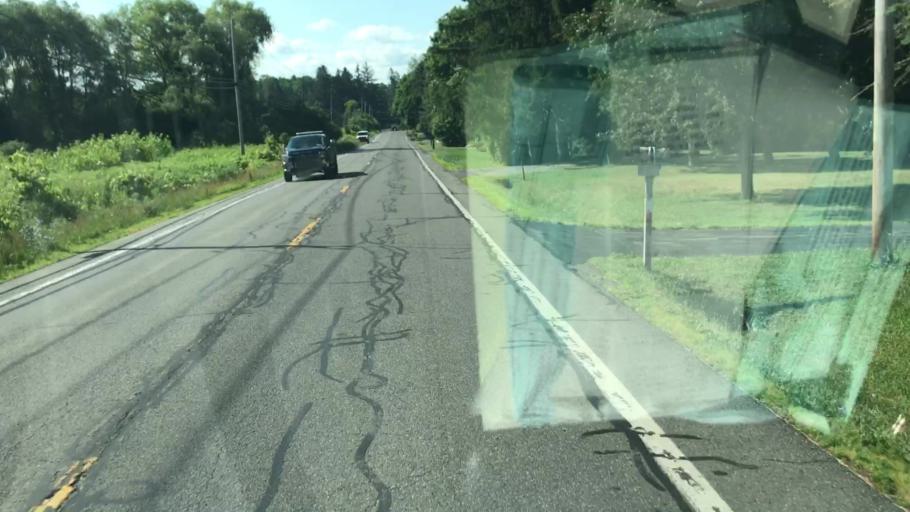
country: US
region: New York
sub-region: Onondaga County
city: Skaneateles
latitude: 42.9287
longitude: -76.4071
